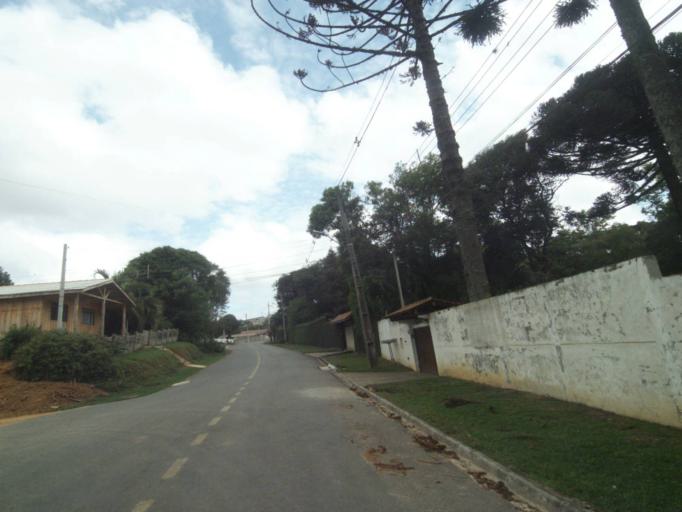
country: BR
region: Parana
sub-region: Curitiba
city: Curitiba
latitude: -25.3775
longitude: -49.2930
